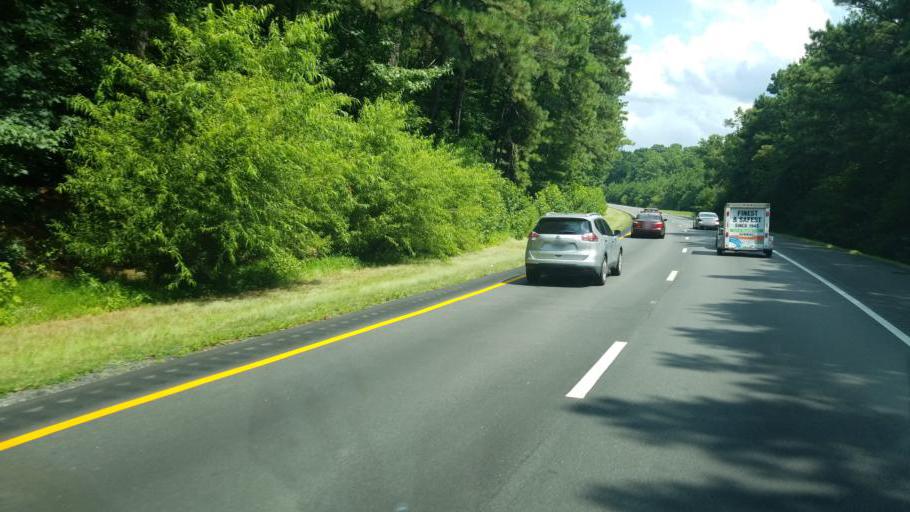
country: US
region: Virginia
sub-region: City of Suffolk
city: Suffolk
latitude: 36.7534
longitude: -76.5293
